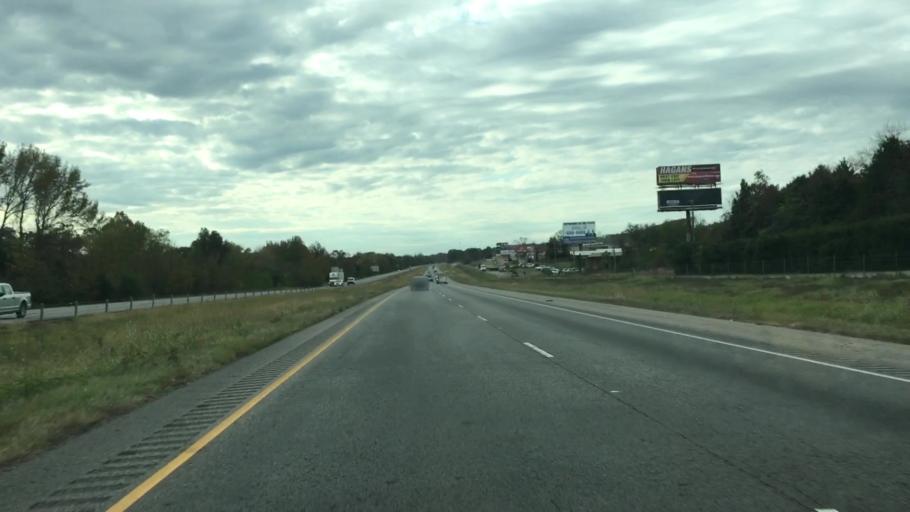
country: US
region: Arkansas
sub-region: Conway County
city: Morrilton
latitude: 35.1627
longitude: -92.6592
